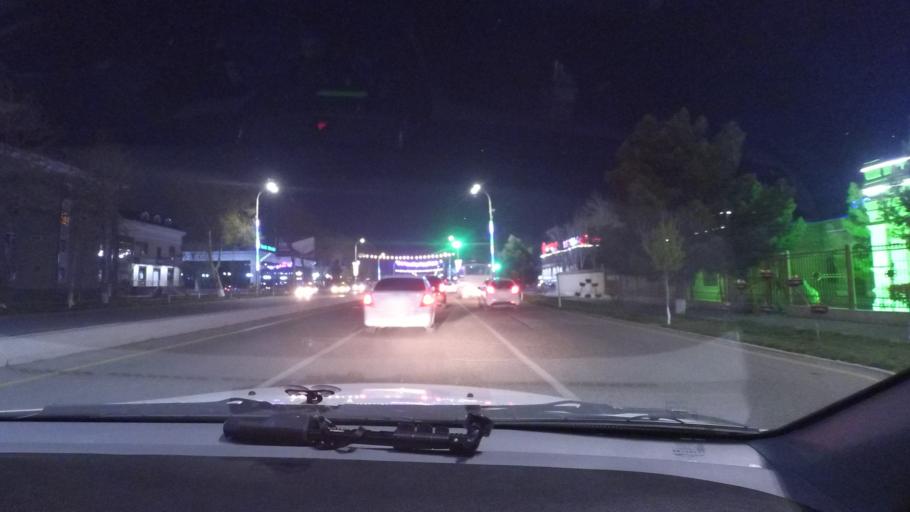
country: UZ
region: Bukhara
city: Bukhara
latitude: 39.7717
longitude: 64.4421
